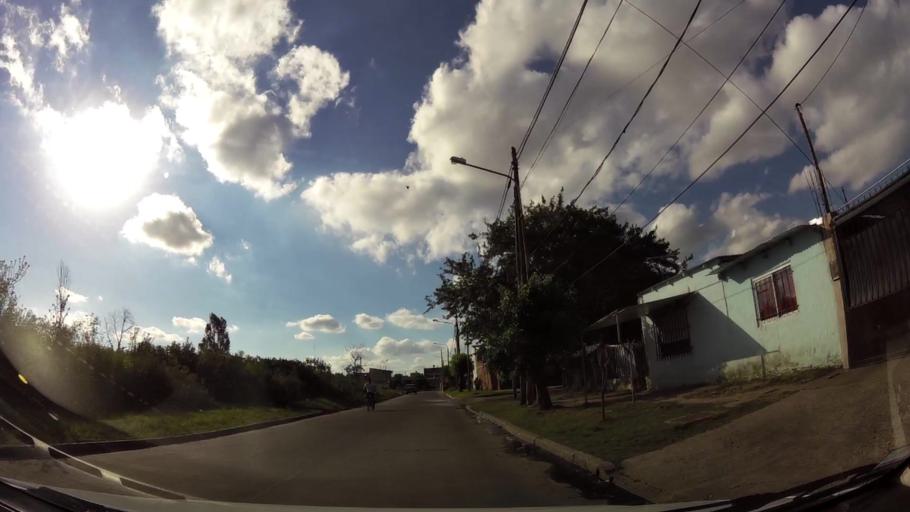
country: AR
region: Buenos Aires
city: San Justo
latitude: -34.6882
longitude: -58.5971
